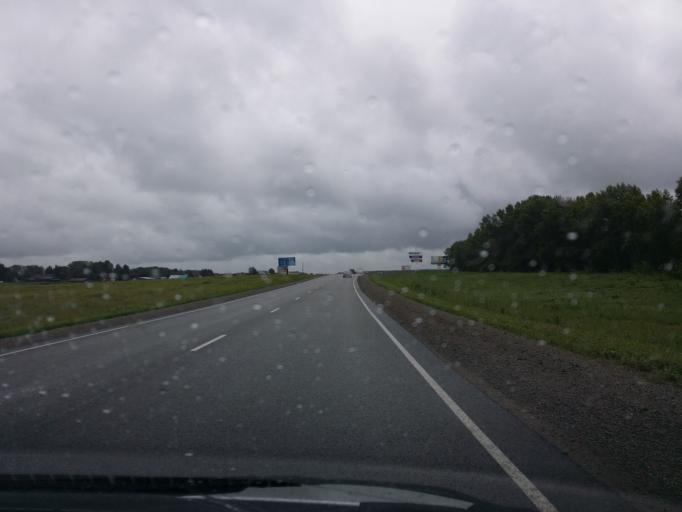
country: RU
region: Altai Krai
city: Zarya
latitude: 52.5907
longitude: 85.1621
